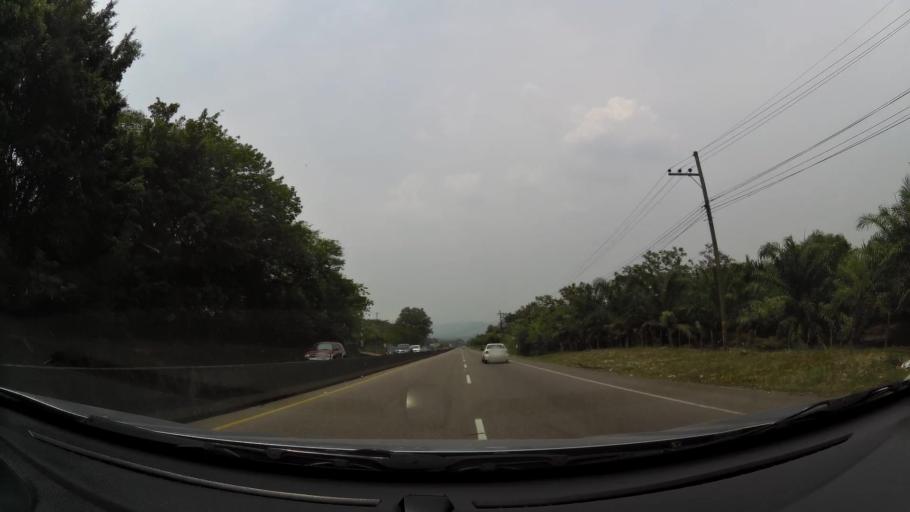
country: HN
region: Cortes
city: Oropendolas
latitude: 15.0027
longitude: -87.9301
